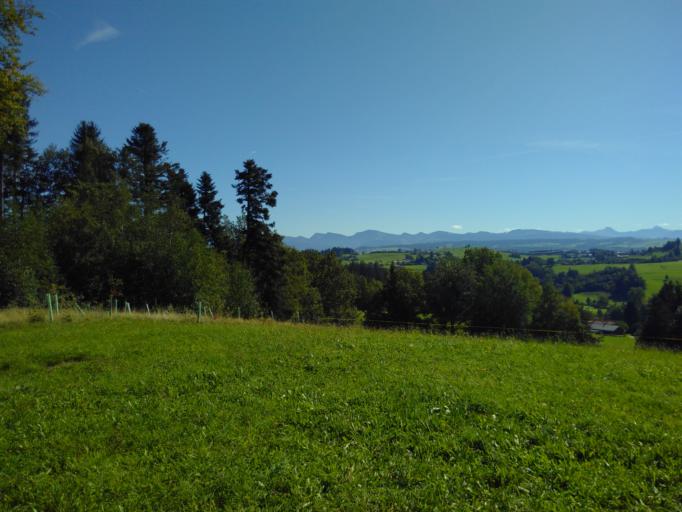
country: DE
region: Bavaria
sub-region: Swabia
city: Scheidegg
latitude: 47.5980
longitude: 9.8415
